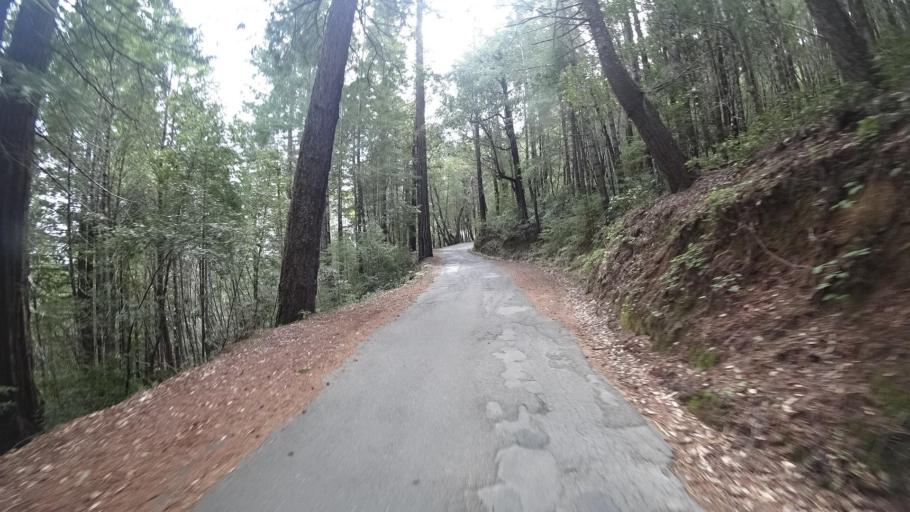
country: US
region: California
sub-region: Humboldt County
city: Redway
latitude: 40.0659
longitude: -123.8304
